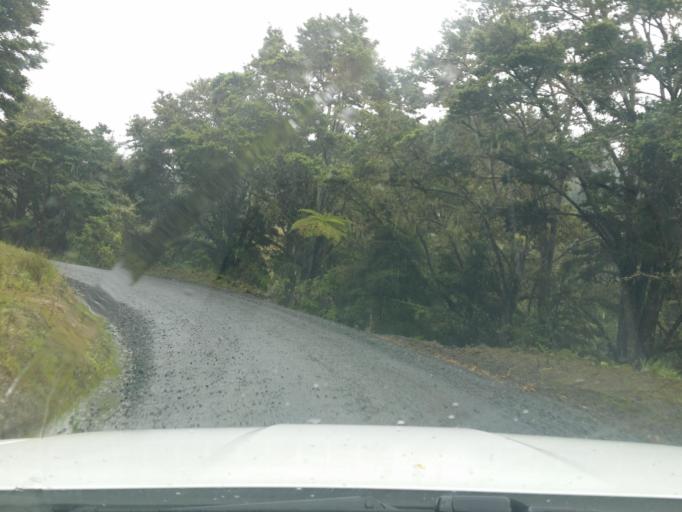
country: NZ
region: Northland
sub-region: Kaipara District
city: Dargaville
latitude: -35.7994
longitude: 173.9907
